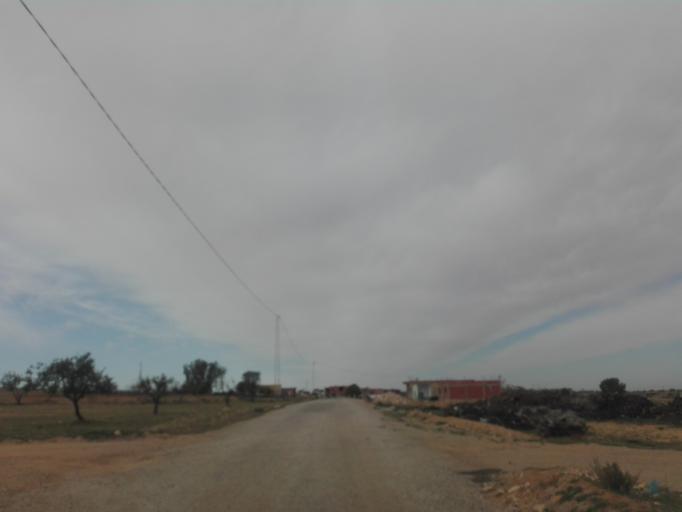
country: TN
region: Safaqis
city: Sfax
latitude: 34.7325
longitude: 10.4964
